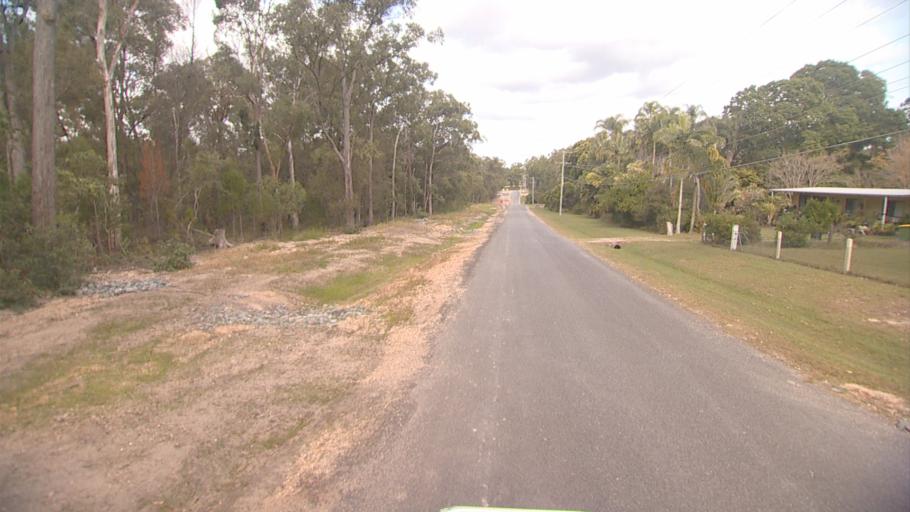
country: AU
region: Queensland
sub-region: Logan
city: Woodridge
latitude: -27.6628
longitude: 153.0669
